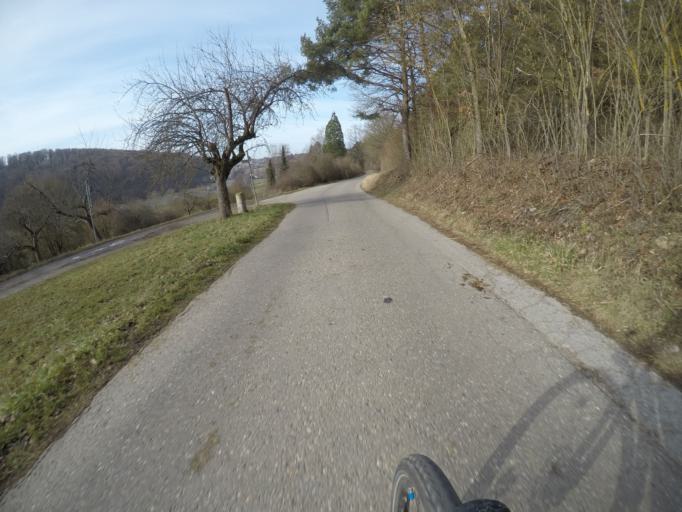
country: DE
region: Baden-Wuerttemberg
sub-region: Karlsruhe Region
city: Gechingen
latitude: 48.6989
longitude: 8.8519
